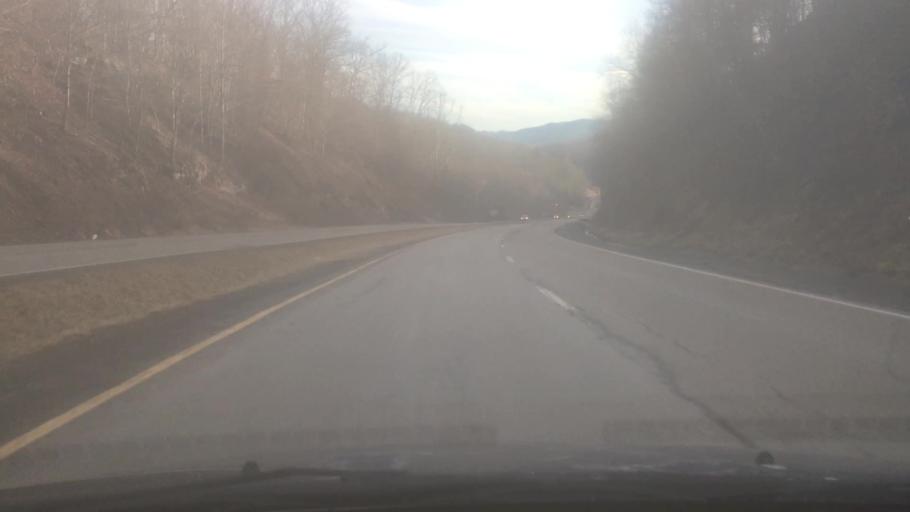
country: US
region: Virginia
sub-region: Wise County
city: Pound
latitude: 37.1066
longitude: -82.5993
